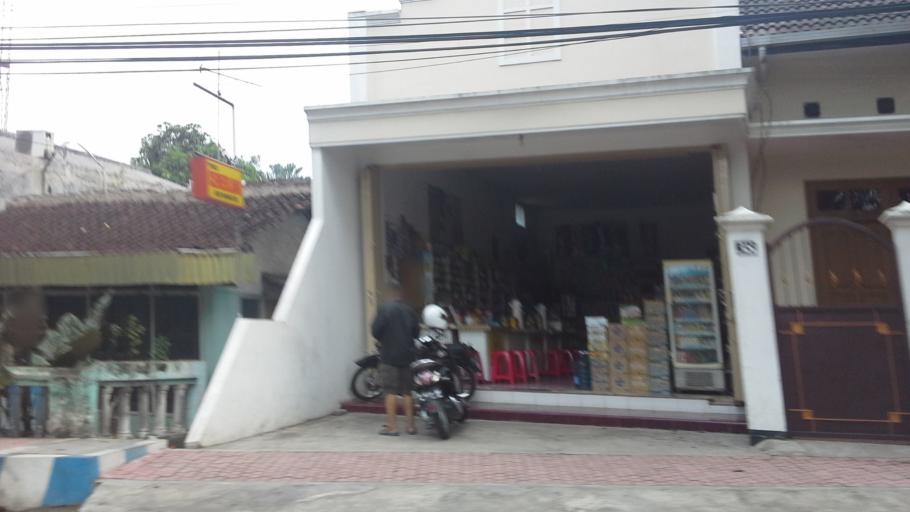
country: ID
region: East Java
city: Bondowoso
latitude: -7.9228
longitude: 113.8194
